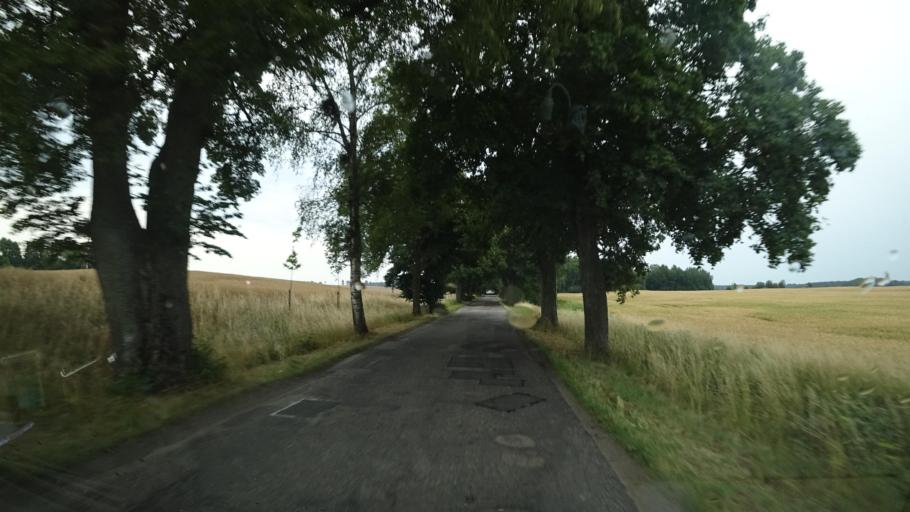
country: PL
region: Warmian-Masurian Voivodeship
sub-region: Powiat gizycki
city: Ryn
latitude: 53.9125
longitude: 21.5590
